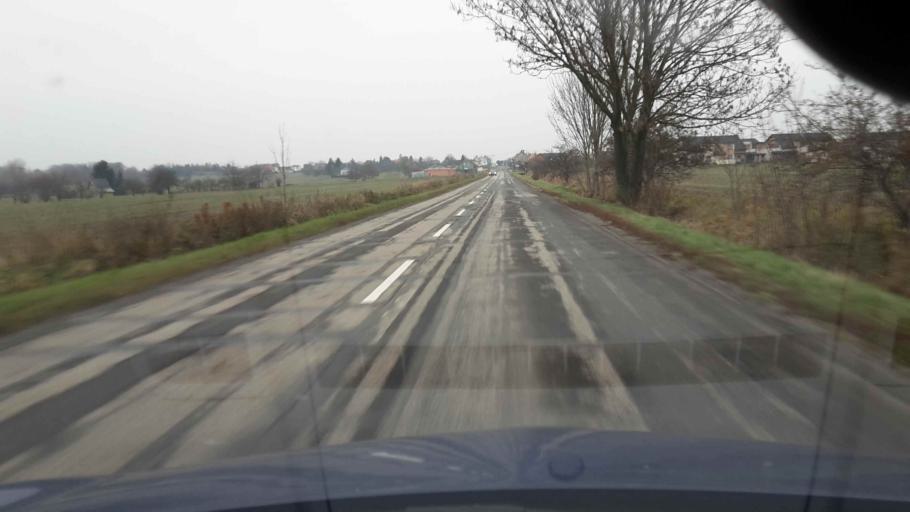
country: CZ
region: Olomoucky
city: Horka nad Moravou
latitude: 49.6085
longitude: 17.2100
